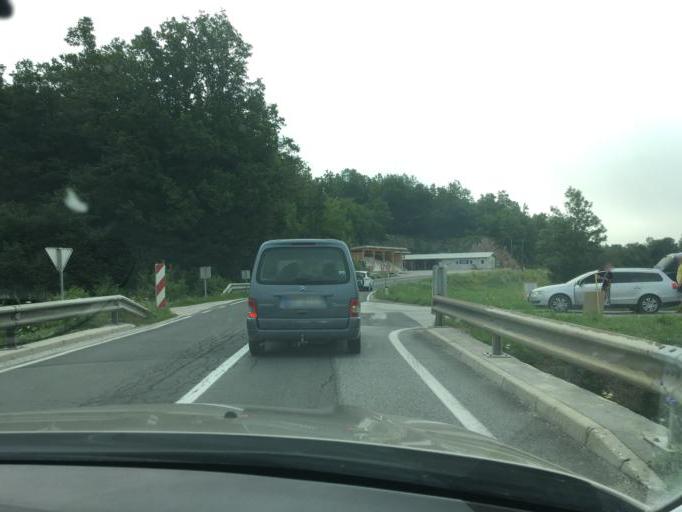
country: SI
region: Ribnica
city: Ribnica
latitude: 45.7641
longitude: 14.6995
